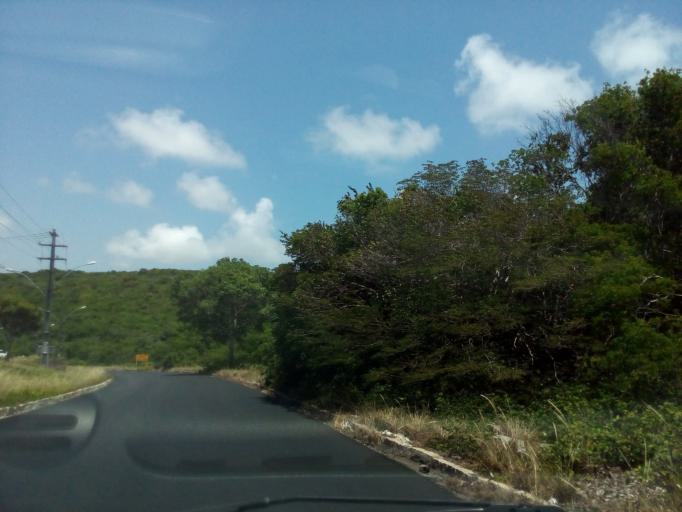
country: BR
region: Rio Grande do Norte
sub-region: Natal
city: Natal
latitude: -5.8412
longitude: -35.1950
